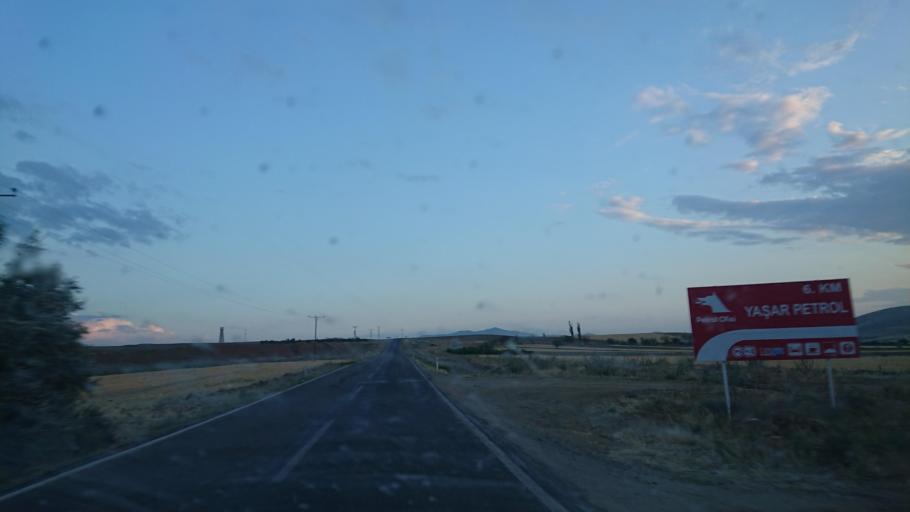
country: TR
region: Aksaray
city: Balci
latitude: 38.8049
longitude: 34.1307
